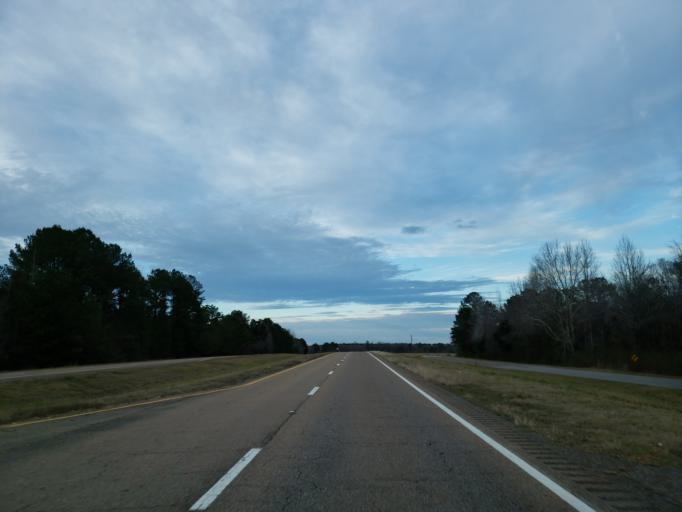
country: US
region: Mississippi
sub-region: Lauderdale County
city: Meridian Station
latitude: 32.5369
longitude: -88.5090
